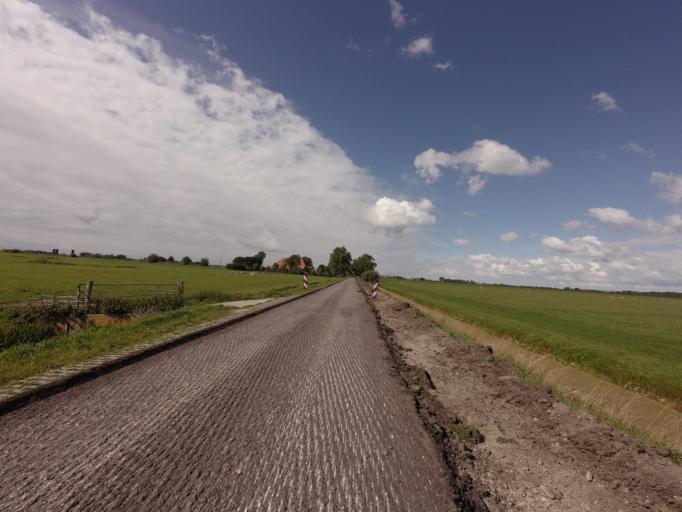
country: NL
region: Friesland
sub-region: Sudwest Fryslan
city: Bolsward
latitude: 53.0338
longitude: 5.5664
